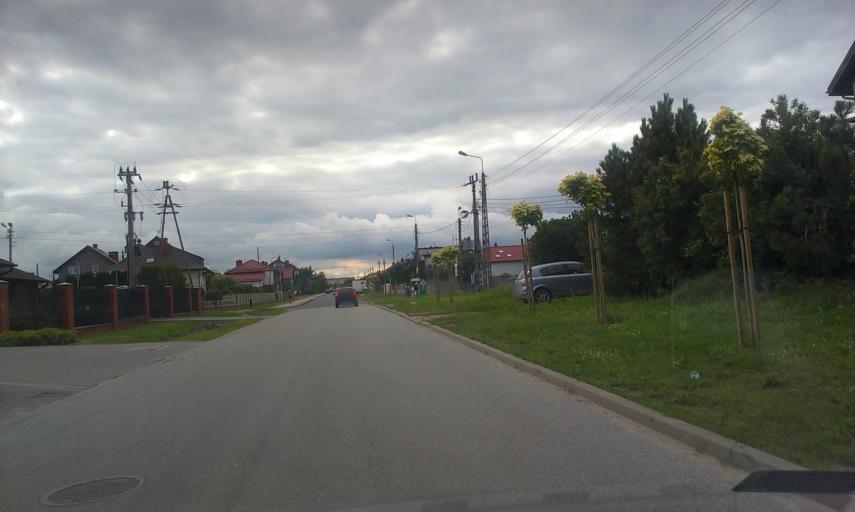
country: PL
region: Masovian Voivodeship
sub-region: Powiat zyrardowski
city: Mszczonow
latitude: 51.9746
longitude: 20.5390
